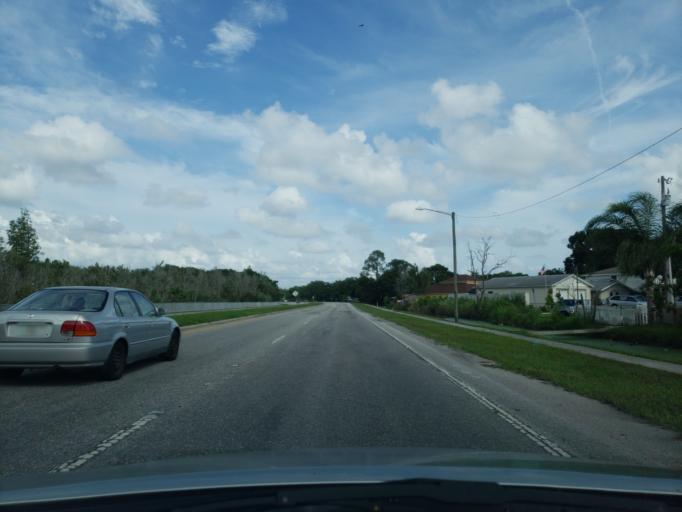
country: US
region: Florida
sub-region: Hillsborough County
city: Egypt Lake-Leto
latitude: 28.0088
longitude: -82.5112
